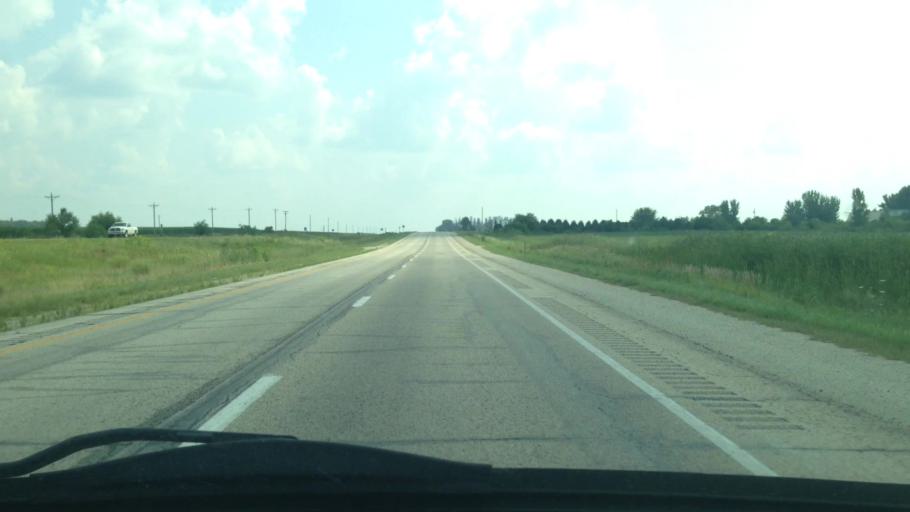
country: US
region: Iowa
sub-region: Bremer County
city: Tripoli
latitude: 42.8662
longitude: -92.3377
